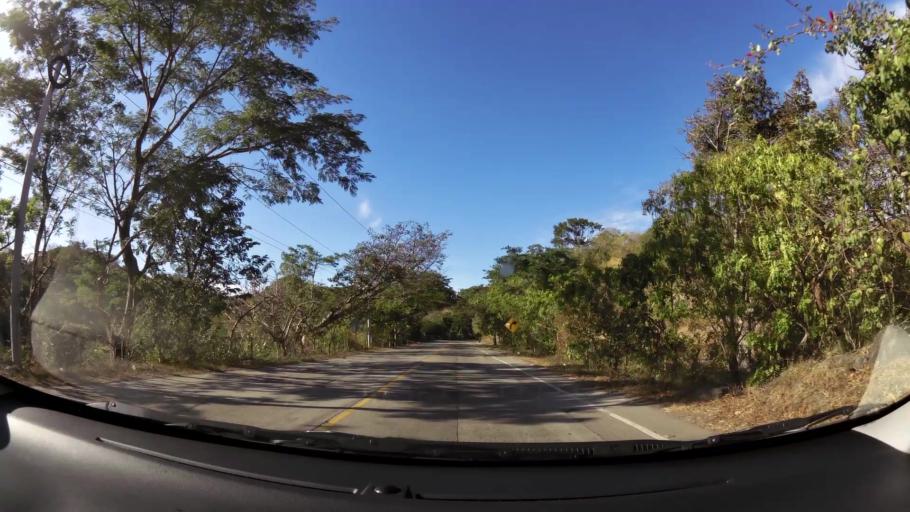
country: SV
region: Santa Ana
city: Texistepeque
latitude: 14.1391
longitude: -89.5132
